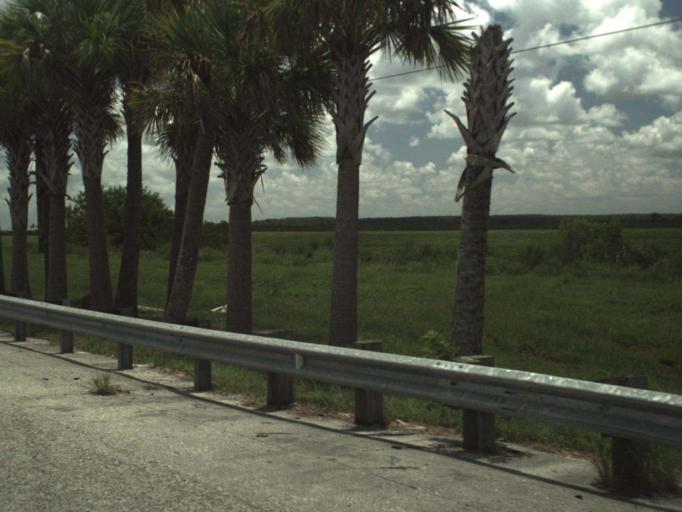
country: US
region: Florida
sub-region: Indian River County
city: Fellsmere
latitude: 27.6417
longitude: -80.7458
